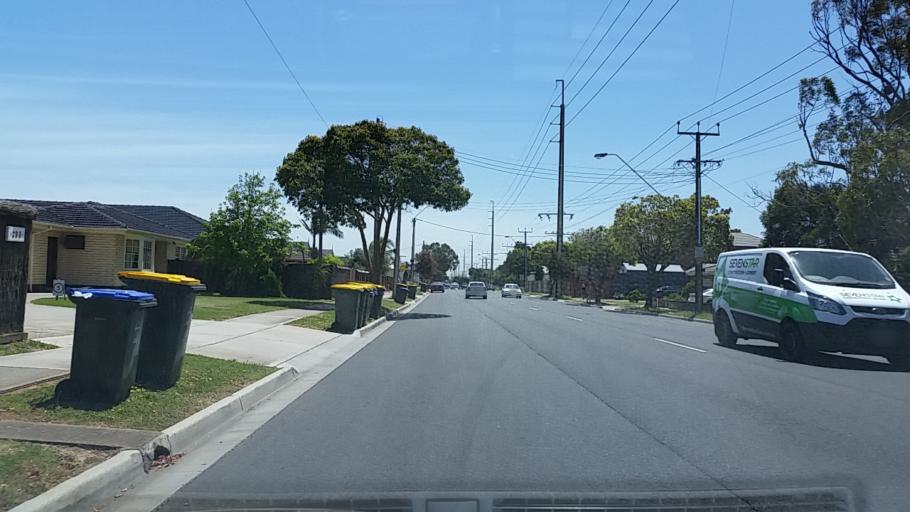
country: AU
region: South Australia
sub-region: Charles Sturt
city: Findon
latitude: -34.9029
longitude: 138.5323
